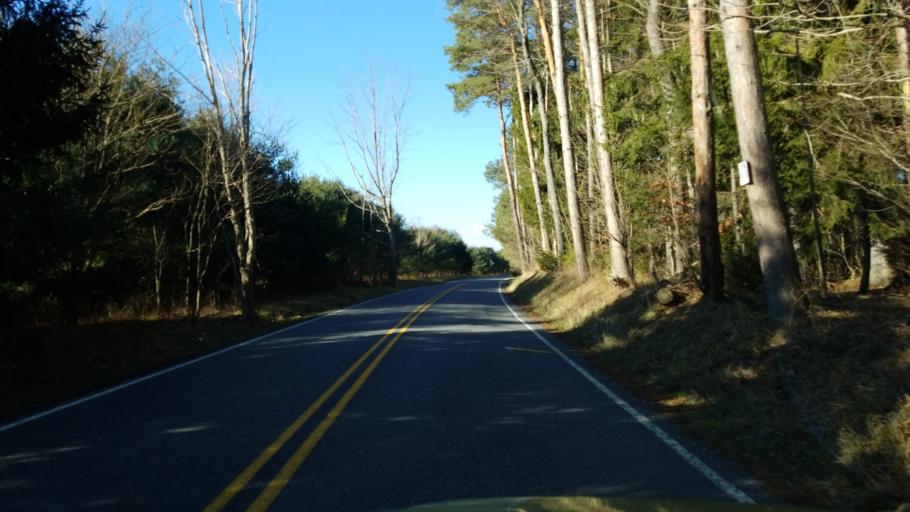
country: US
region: Pennsylvania
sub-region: Clearfield County
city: Hyde
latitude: 40.9757
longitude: -78.4620
